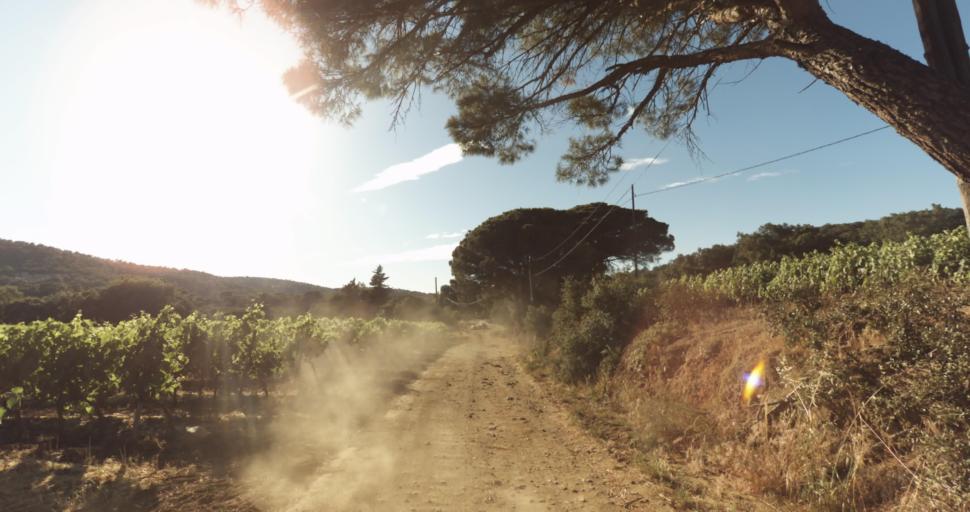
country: FR
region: Provence-Alpes-Cote d'Azur
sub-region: Departement du Var
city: La Croix-Valmer
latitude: 43.2204
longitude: 6.5621
